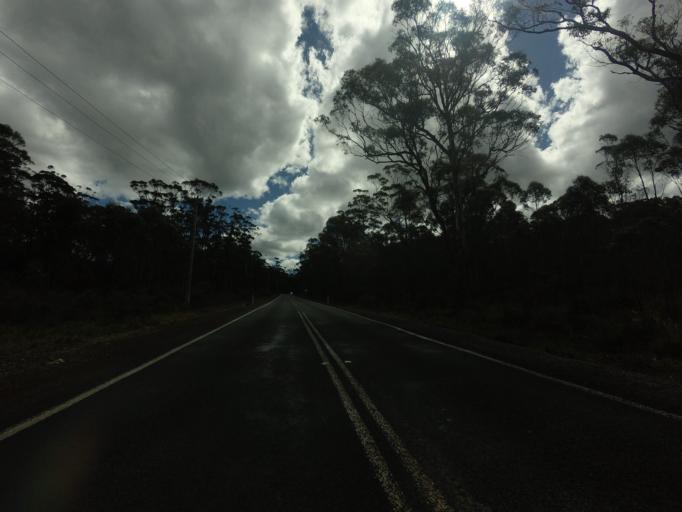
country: AU
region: Tasmania
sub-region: Northern Midlands
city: Evandale
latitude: -42.0128
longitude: 147.7306
